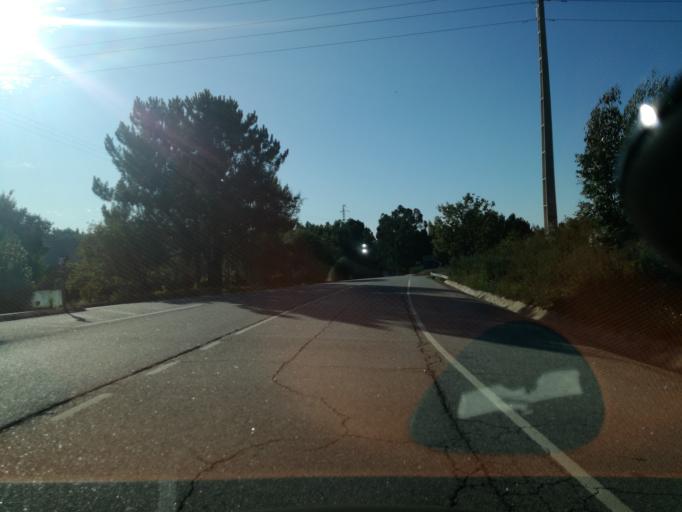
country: PT
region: Porto
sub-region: Santo Tirso
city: Sao Miguel do Couto
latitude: 41.3147
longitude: -8.4677
